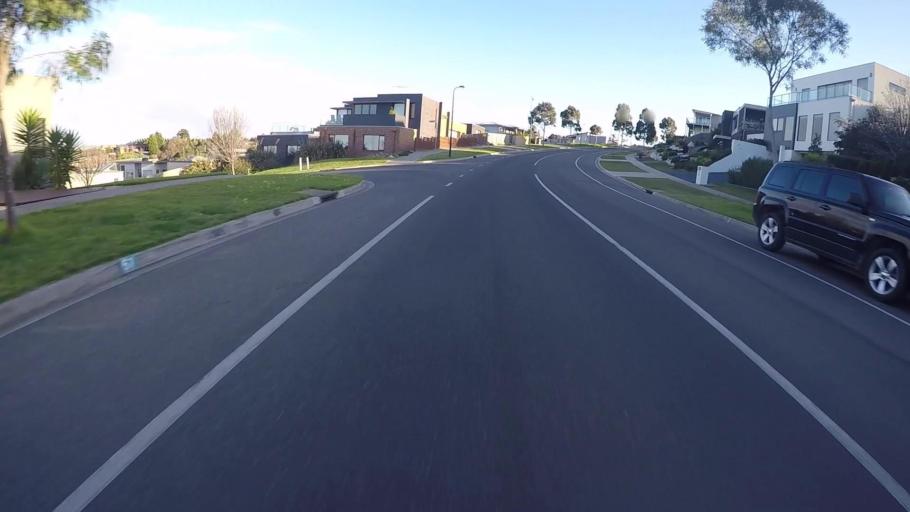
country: AU
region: Victoria
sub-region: Greater Geelong
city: Wandana Heights
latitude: -38.1687
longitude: 144.3021
